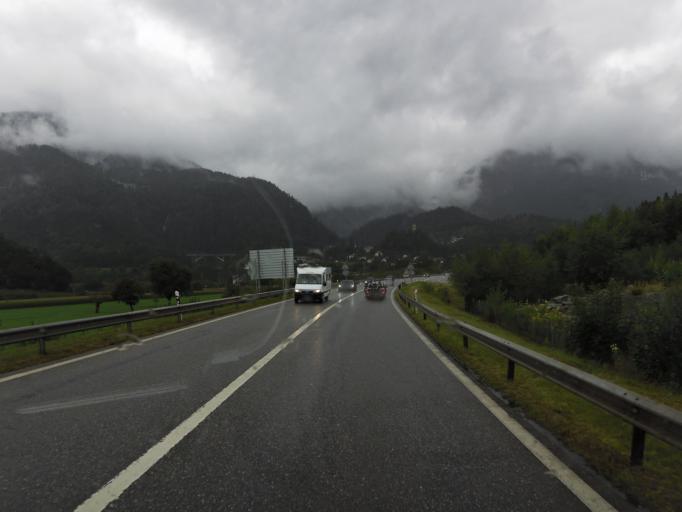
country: CH
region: Grisons
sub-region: Imboden District
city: Bonaduz
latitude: 46.8186
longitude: 9.4057
